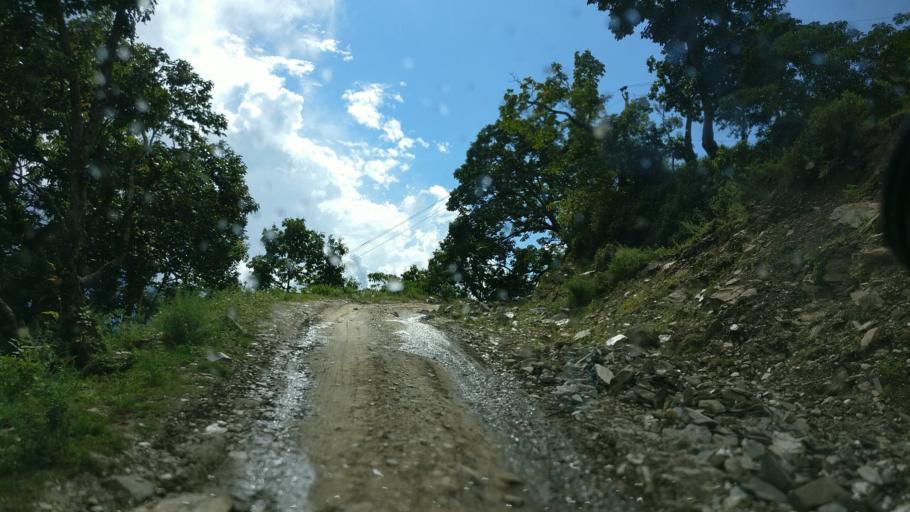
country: NP
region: Western Region
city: Baglung
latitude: 28.2747
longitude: 83.6426
